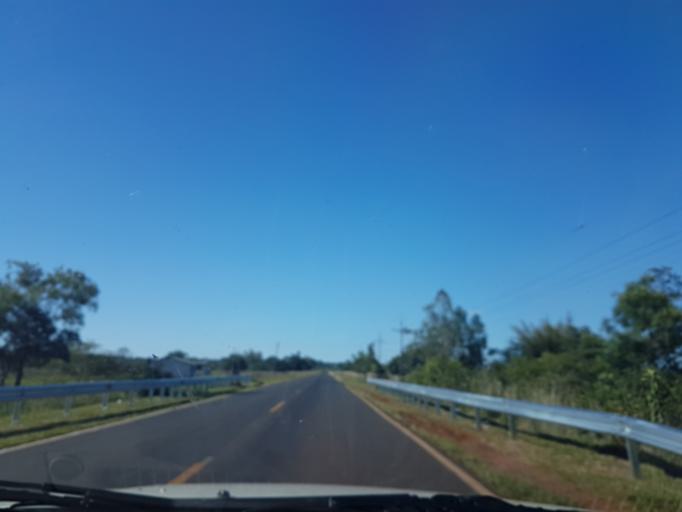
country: PY
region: Cordillera
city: Arroyos y Esteros
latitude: -25.0987
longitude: -57.0936
